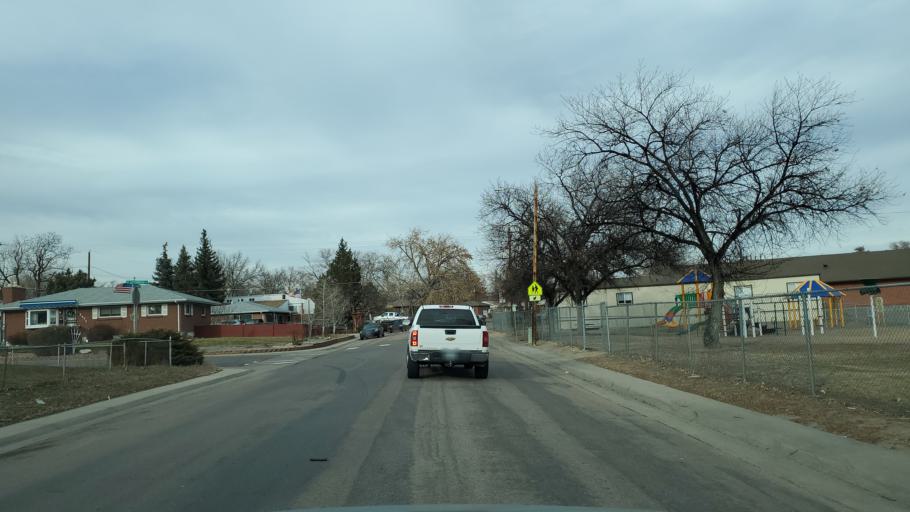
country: US
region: Colorado
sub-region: Adams County
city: Westminster
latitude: 39.8382
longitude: -105.0209
